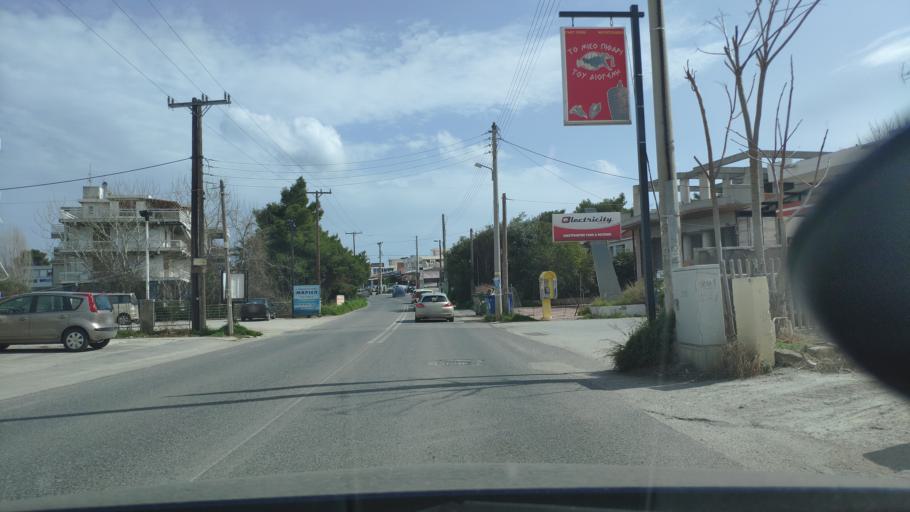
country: GR
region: Attica
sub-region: Nomarchia Anatolikis Attikis
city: Limin Mesoyaias
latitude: 37.8859
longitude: 24.0056
